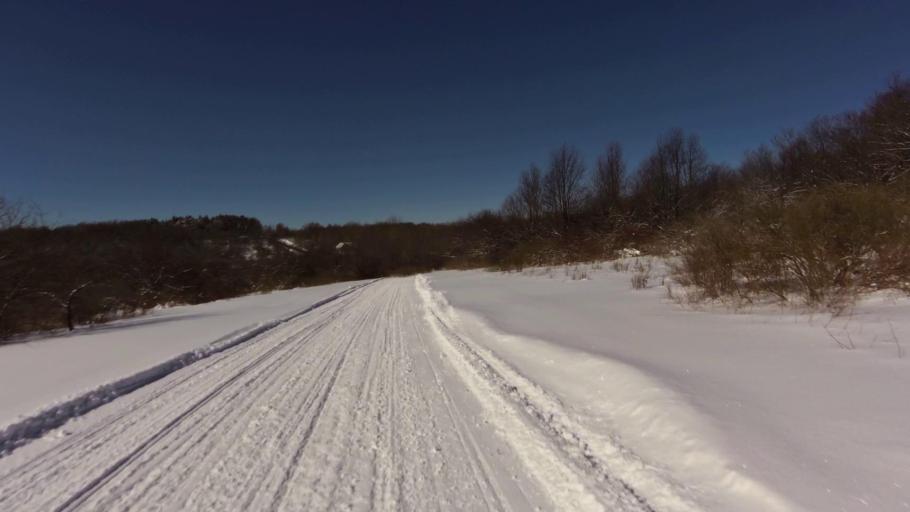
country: US
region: New York
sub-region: Chautauqua County
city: Lakewood
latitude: 42.2271
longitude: -79.3444
